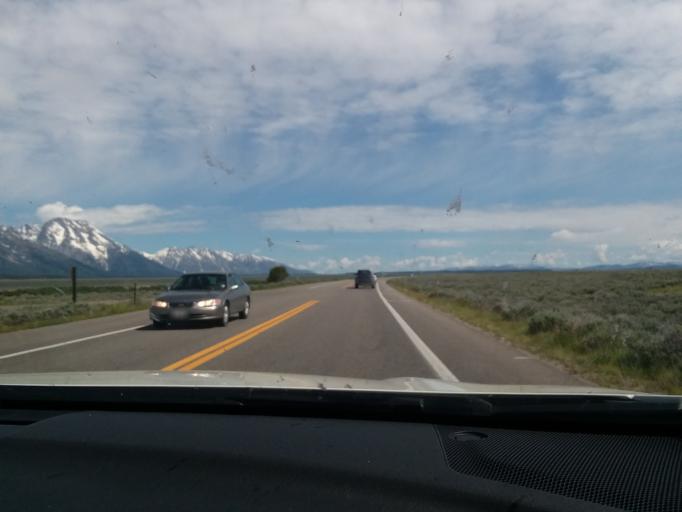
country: US
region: Wyoming
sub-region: Teton County
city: Jackson
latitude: 43.6913
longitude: -110.6722
